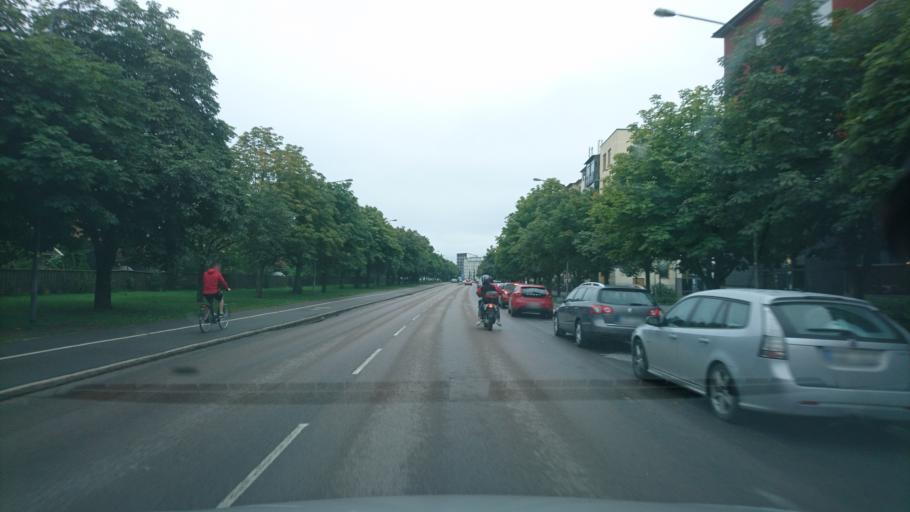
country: SE
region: Uppsala
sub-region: Uppsala Kommun
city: Uppsala
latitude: 59.8710
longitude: 17.6394
